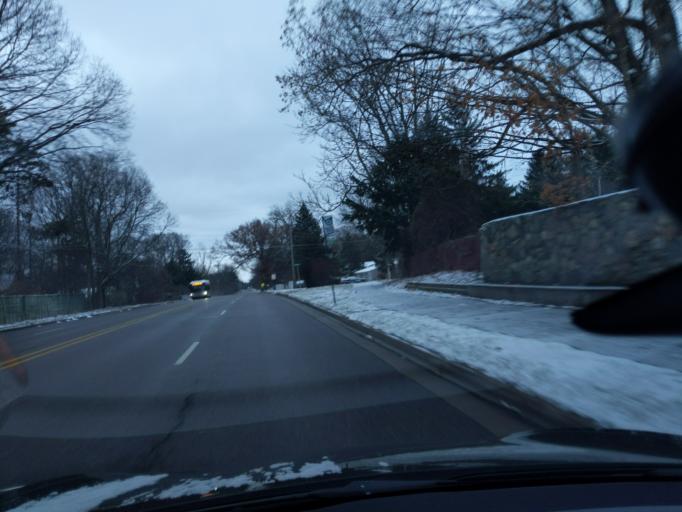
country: US
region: Michigan
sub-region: Ingham County
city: Okemos
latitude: 42.7118
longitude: -84.4543
